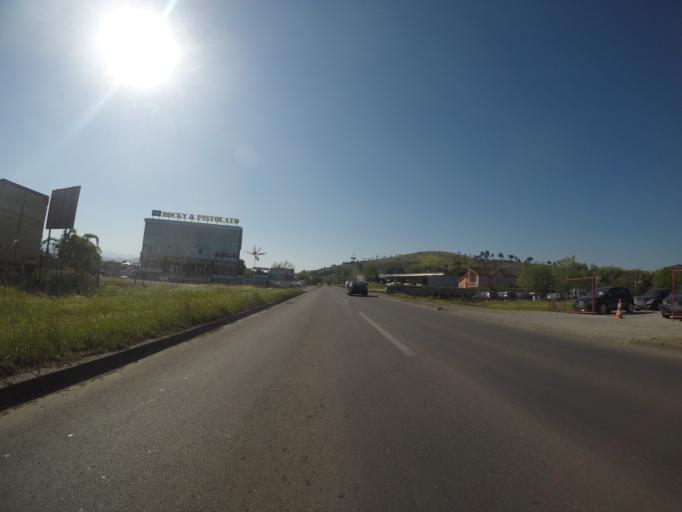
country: ME
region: Podgorica
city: Podgorica
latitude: 42.4272
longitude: 19.2334
